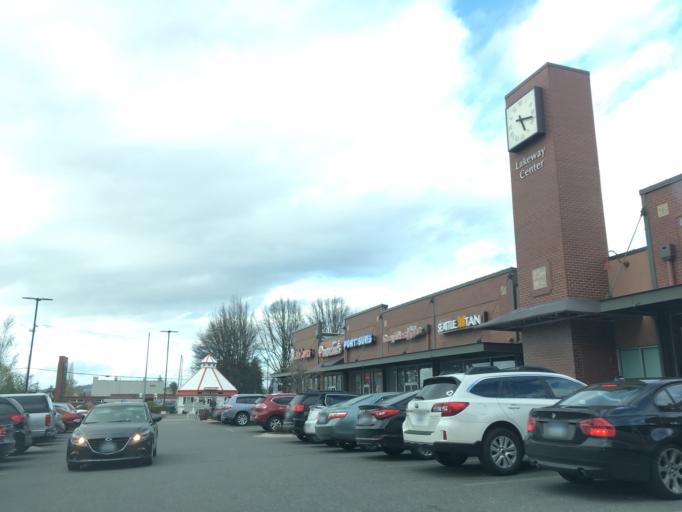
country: US
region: Washington
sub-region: Whatcom County
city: Bellingham
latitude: 48.7439
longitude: -122.4613
